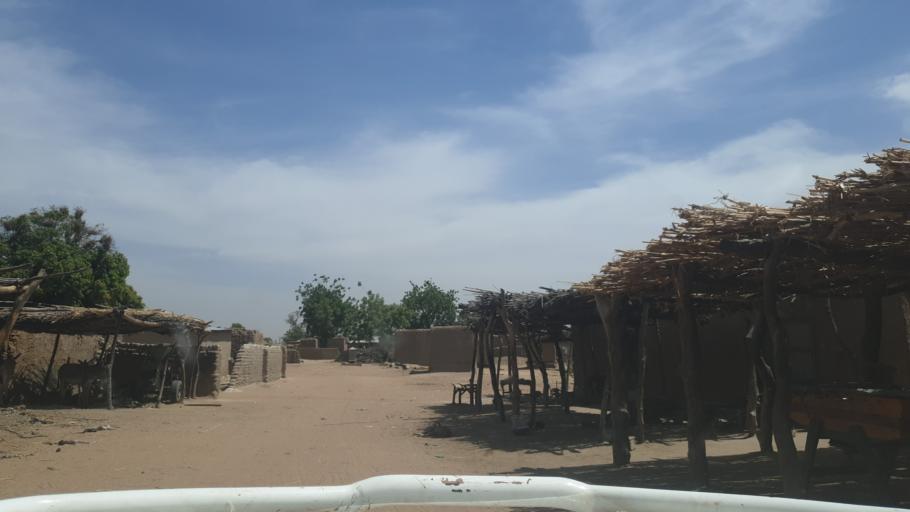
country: ML
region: Sikasso
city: Yorosso
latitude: 12.2915
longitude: -4.6482
